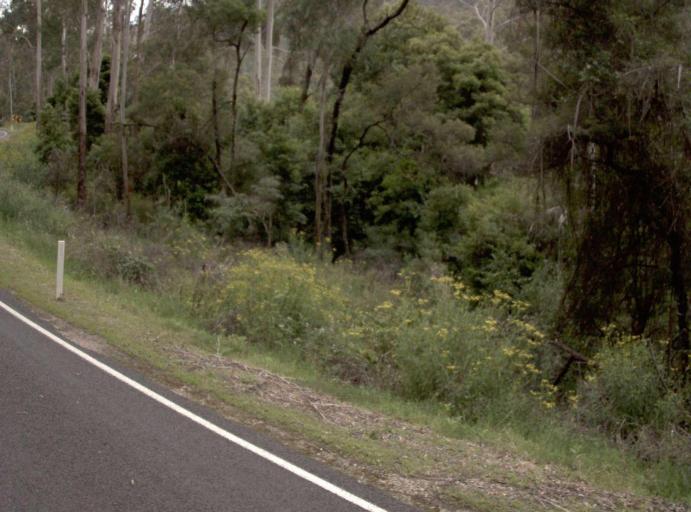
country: AU
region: New South Wales
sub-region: Bombala
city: Bombala
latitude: -37.4175
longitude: 149.1983
